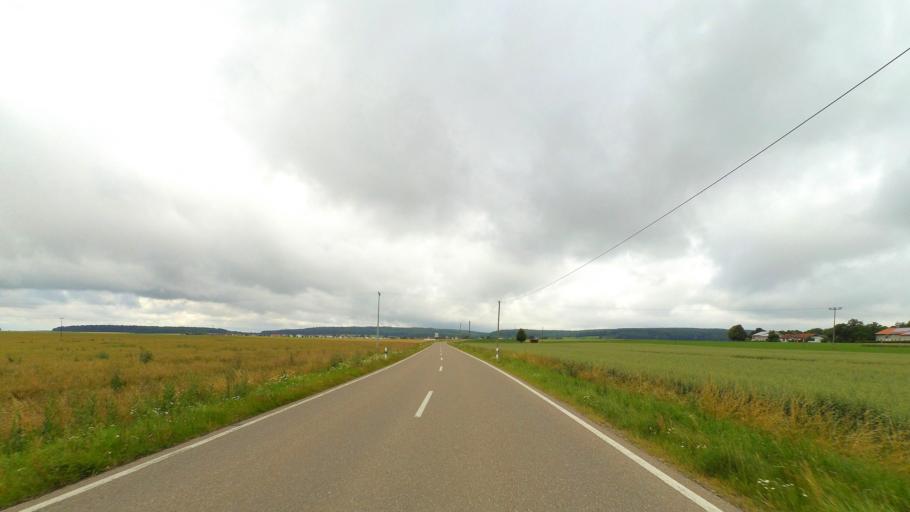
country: DE
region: Baden-Wuerttemberg
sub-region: Tuebingen Region
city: Neenstetten
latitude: 48.5517
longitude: 10.0155
